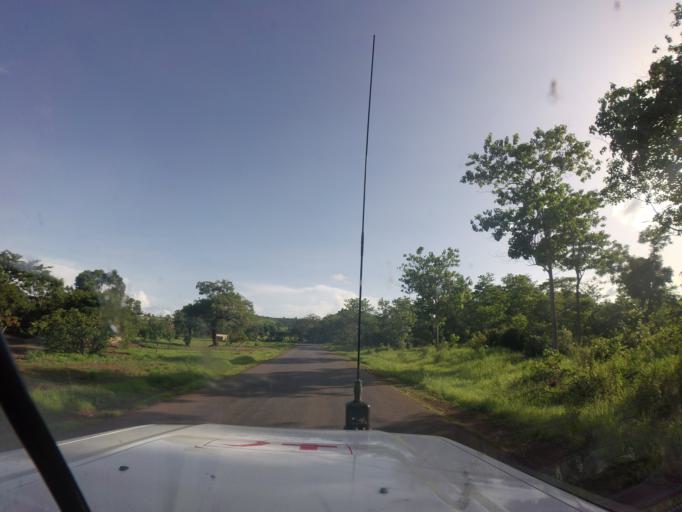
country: GN
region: Kindia
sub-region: Kindia
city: Kindia
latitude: 10.0031
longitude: -12.7050
